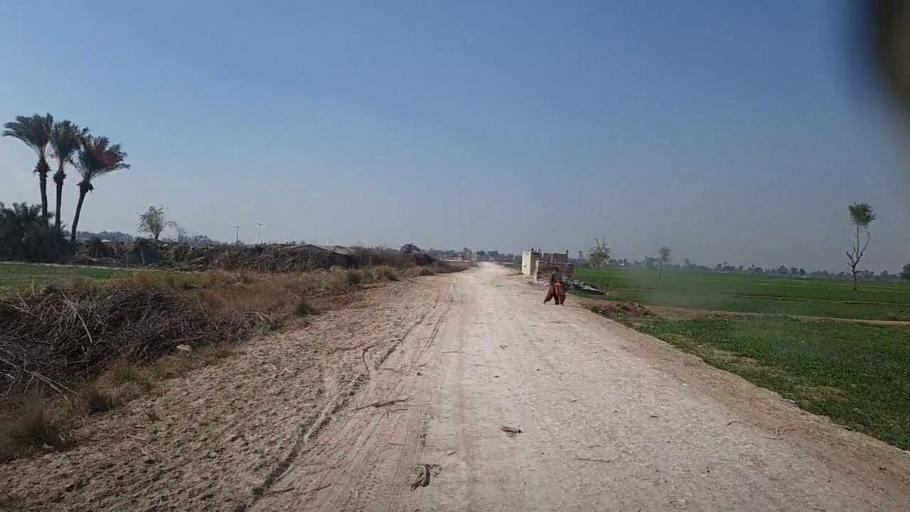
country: PK
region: Sindh
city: Khairpur
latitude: 28.0235
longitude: 69.7448
